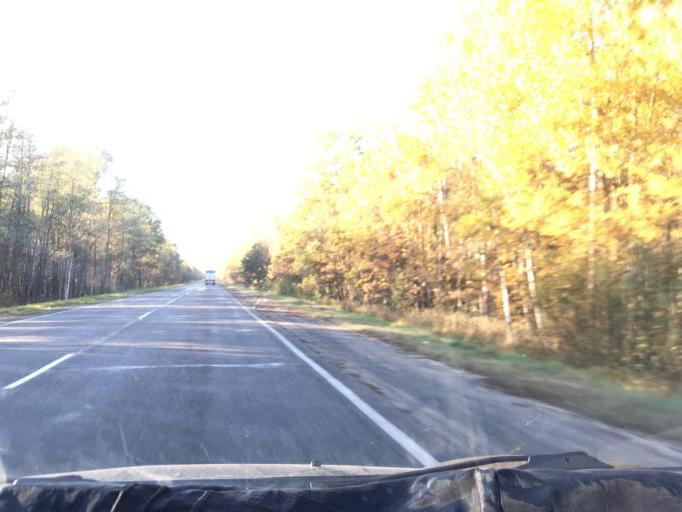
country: BY
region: Gomel
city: Mazyr
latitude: 52.1907
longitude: 29.1249
